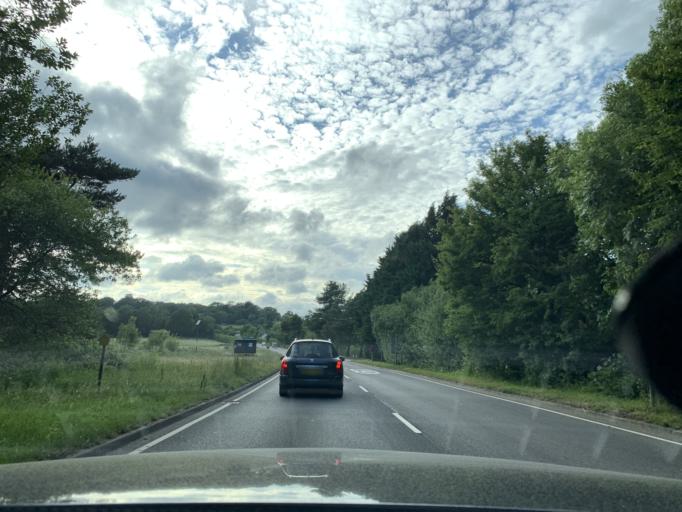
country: GB
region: England
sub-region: East Sussex
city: Robertsbridge
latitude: 50.9602
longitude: 0.4894
